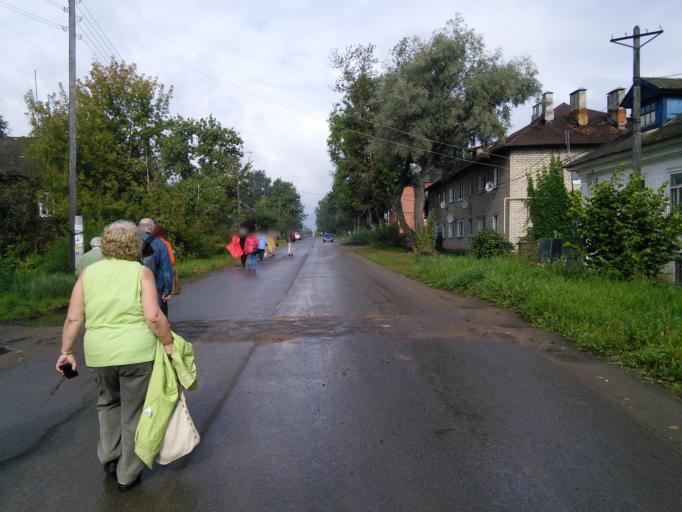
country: RU
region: Jaroslavl
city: Tutayev
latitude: 57.8822
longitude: 39.5465
